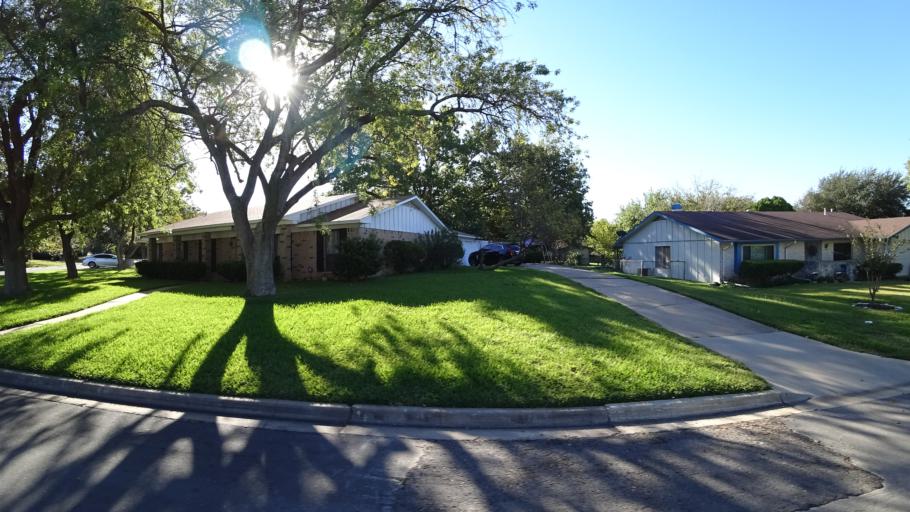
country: US
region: Texas
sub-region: Travis County
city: Austin
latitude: 30.3076
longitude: -97.6642
